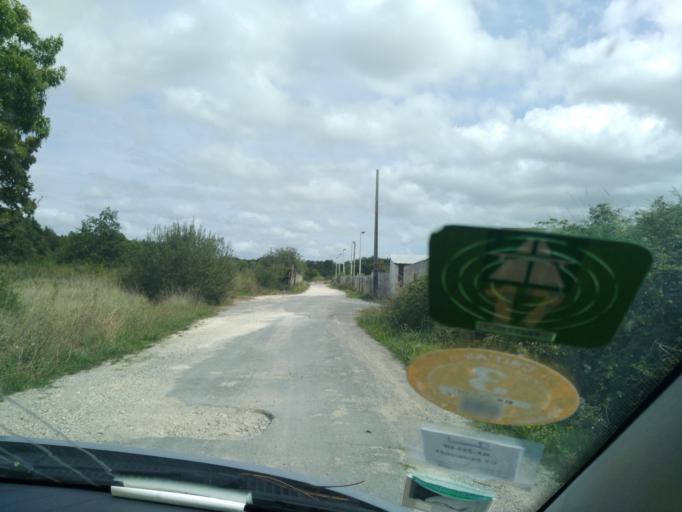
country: FR
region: Poitou-Charentes
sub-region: Departement de la Charente-Maritime
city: Chaillevette
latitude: 45.7139
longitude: -1.0728
